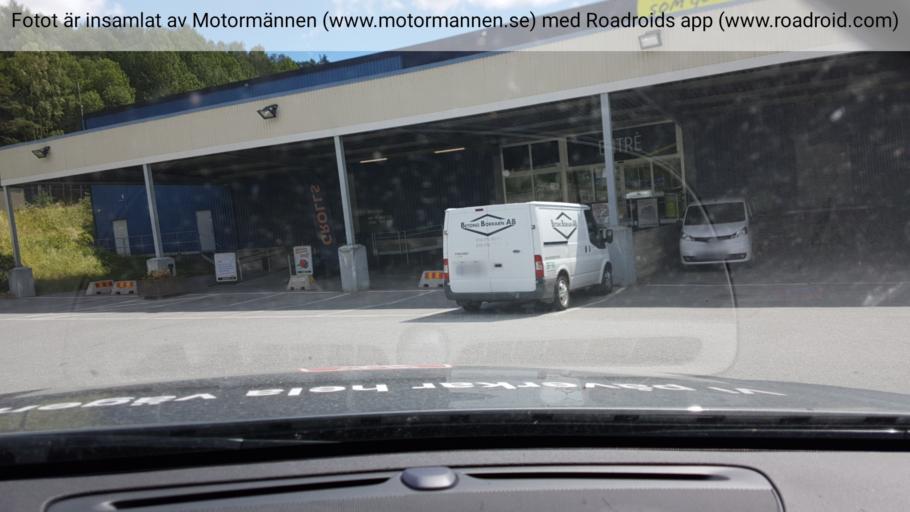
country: SE
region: Stockholm
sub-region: Jarfalla Kommun
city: Jakobsberg
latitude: 59.4046
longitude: 17.8430
